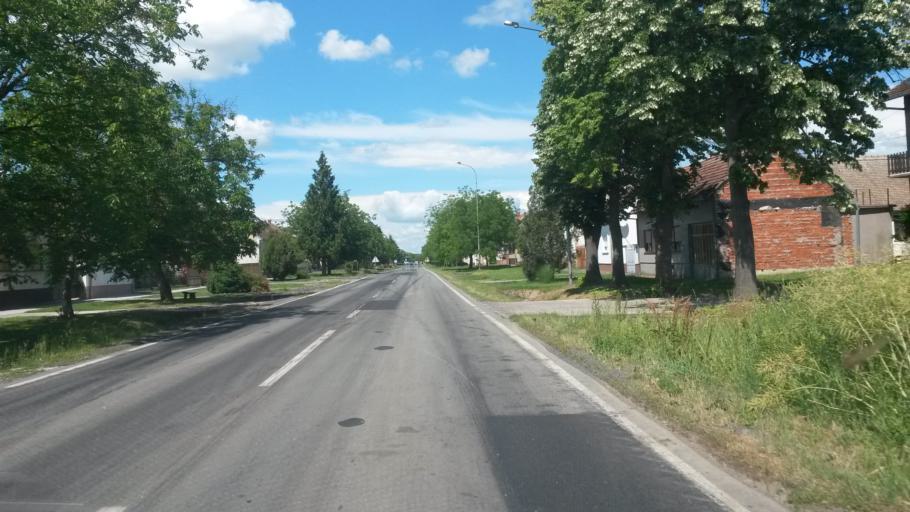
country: HR
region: Osjecko-Baranjska
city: Vuka
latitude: 45.4329
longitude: 18.5040
